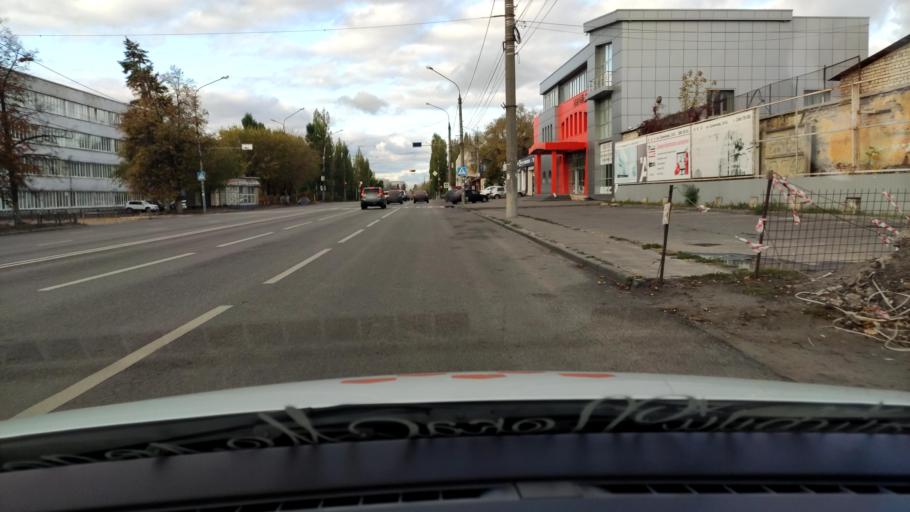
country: RU
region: Voronezj
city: Voronezh
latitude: 51.6862
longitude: 39.1656
